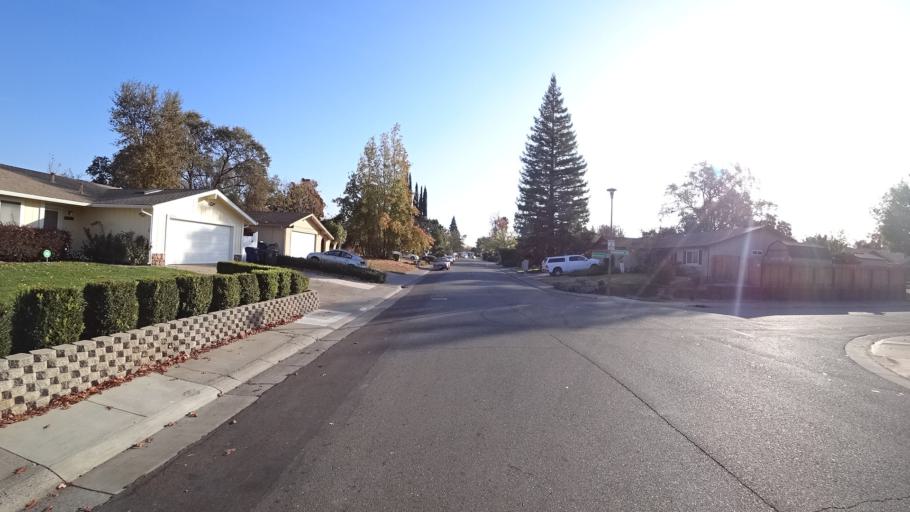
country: US
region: California
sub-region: Sacramento County
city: Citrus Heights
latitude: 38.6962
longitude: -121.2620
